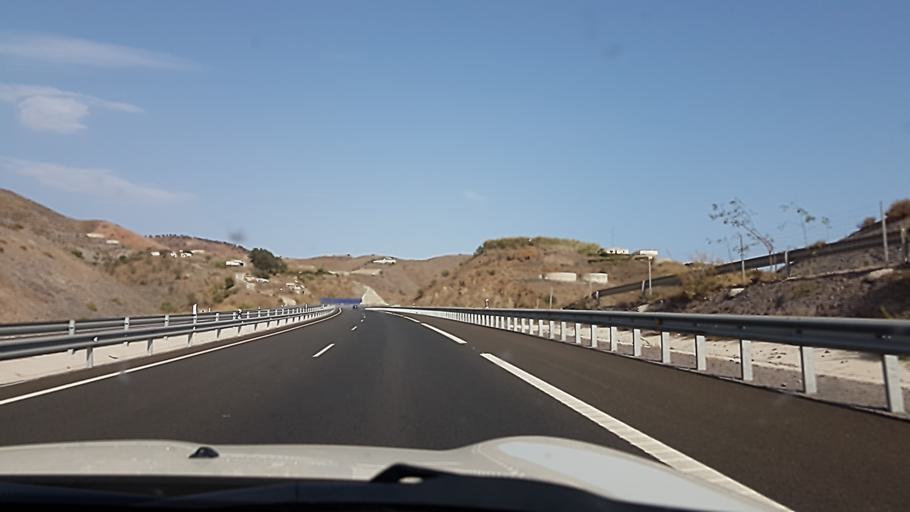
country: ES
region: Andalusia
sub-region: Provincia de Granada
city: Albunol
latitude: 36.7556
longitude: -3.2288
